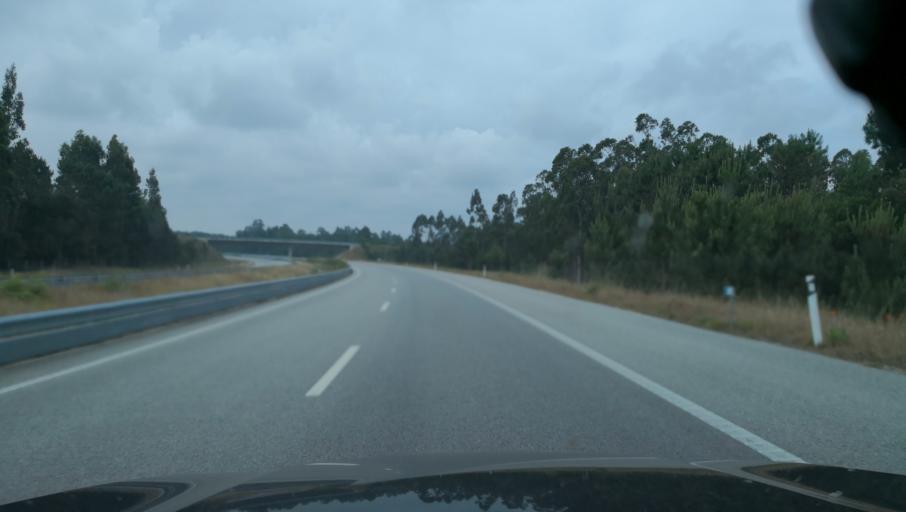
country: PT
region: Coimbra
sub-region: Figueira da Foz
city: Alhadas
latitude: 40.2487
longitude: -8.7793
